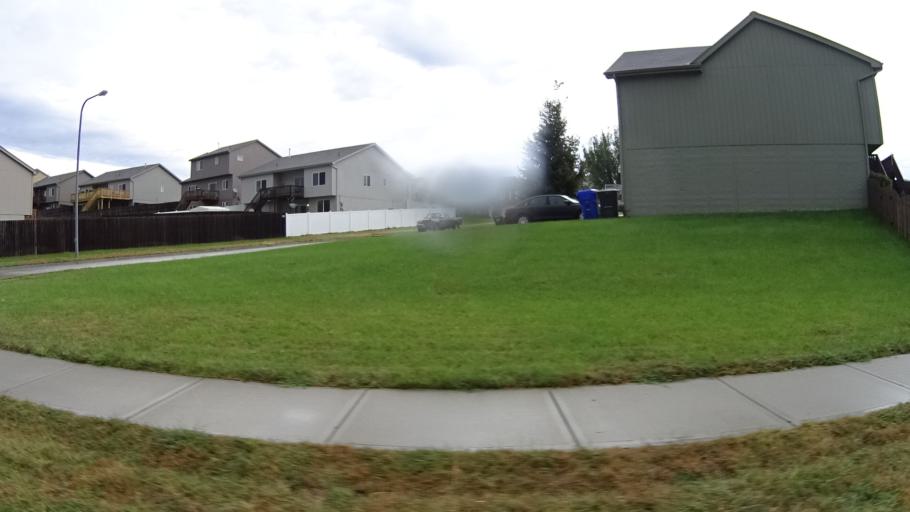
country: US
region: Nebraska
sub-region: Sarpy County
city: Offutt Air Force Base
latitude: 41.1528
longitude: -95.9504
